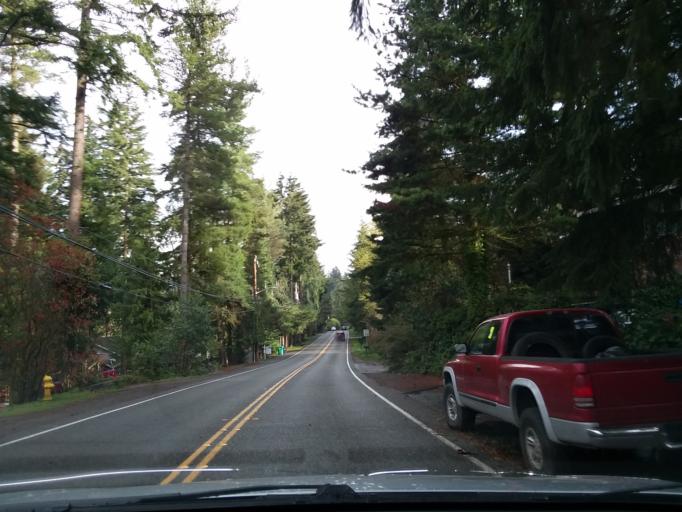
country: US
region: Washington
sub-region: Snohomish County
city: Mountlake Terrace
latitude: 47.7617
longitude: -122.3113
